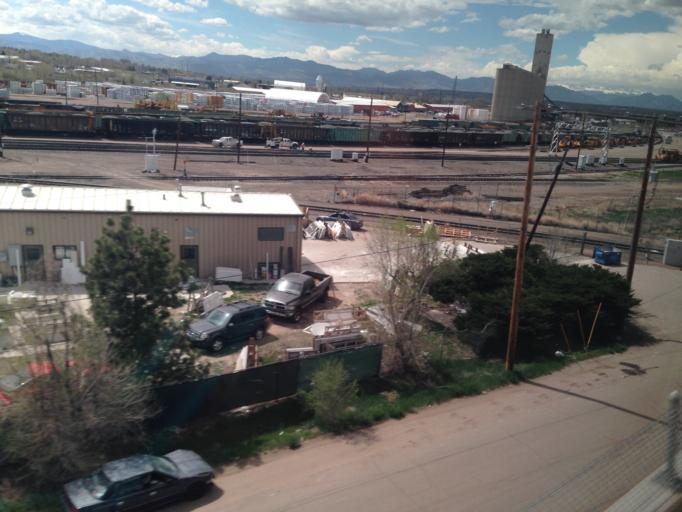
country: US
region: Colorado
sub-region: Adams County
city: Twin Lakes
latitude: 39.8000
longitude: -104.9978
